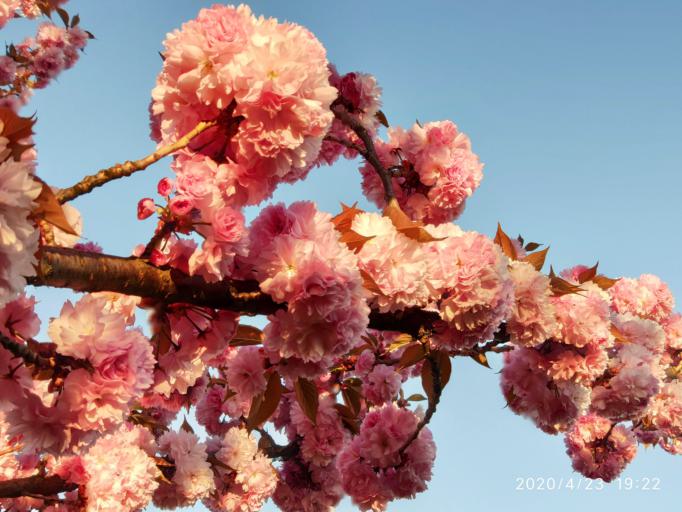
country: PL
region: Lesser Poland Voivodeship
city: Sulecin
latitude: 52.4466
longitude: 15.1139
